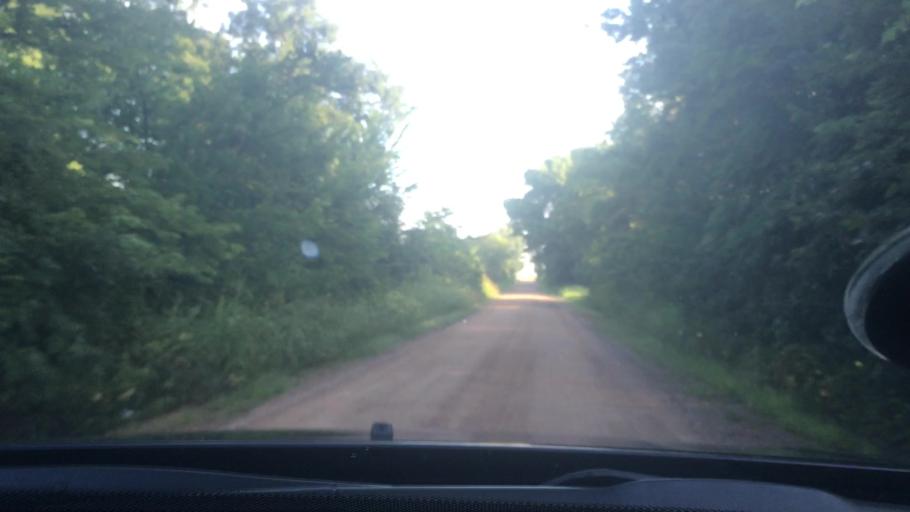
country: US
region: Oklahoma
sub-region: Pontotoc County
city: Ada
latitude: 34.8117
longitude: -96.7749
